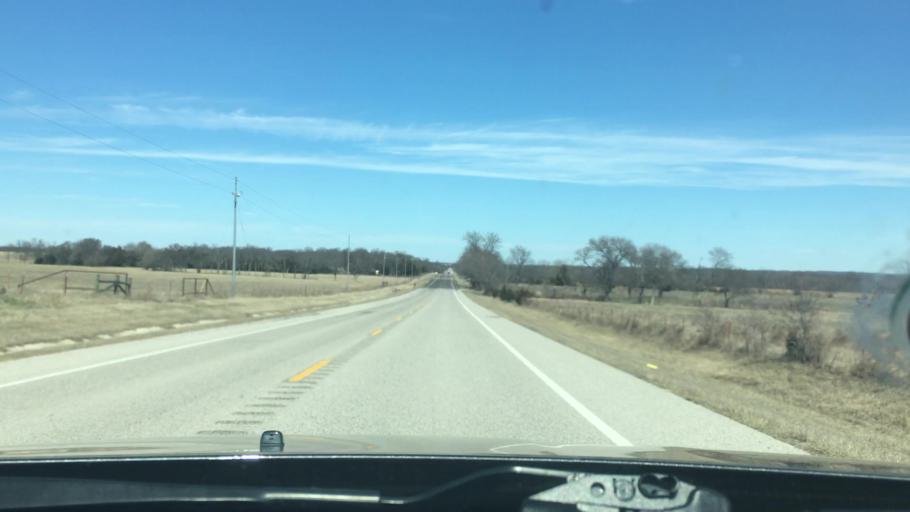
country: US
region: Oklahoma
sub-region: Murray County
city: Sulphur
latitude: 34.3502
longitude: -96.9509
